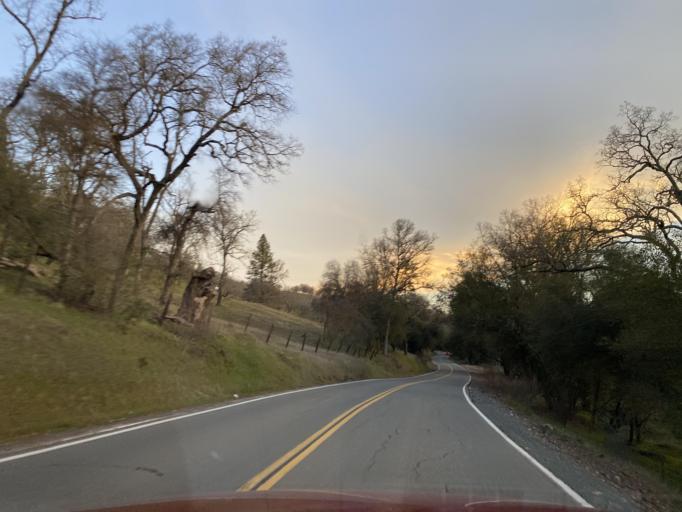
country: US
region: California
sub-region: Amador County
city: Plymouth
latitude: 38.4951
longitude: -120.7893
